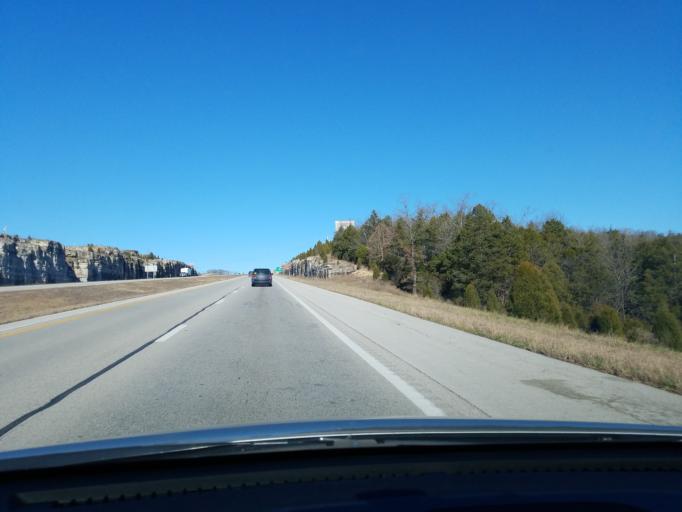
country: US
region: Missouri
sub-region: Taney County
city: Merriam Woods
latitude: 36.7397
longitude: -93.2215
